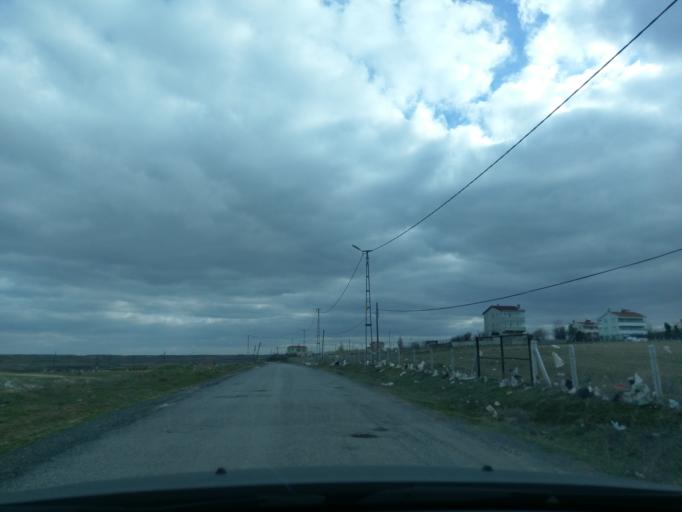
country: TR
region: Istanbul
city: Durusu
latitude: 41.3251
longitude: 28.7266
